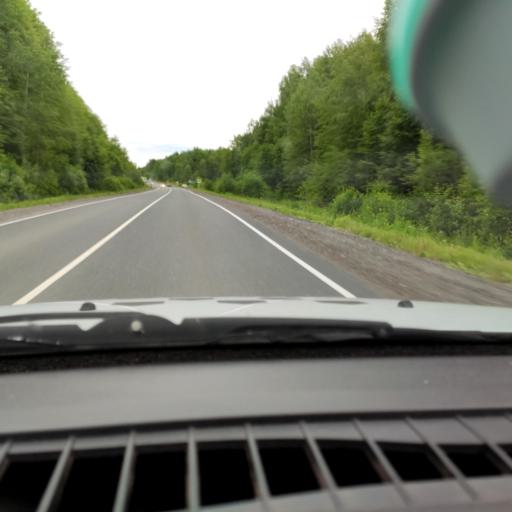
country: RU
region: Perm
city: Lys'va
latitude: 58.1910
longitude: 57.7959
